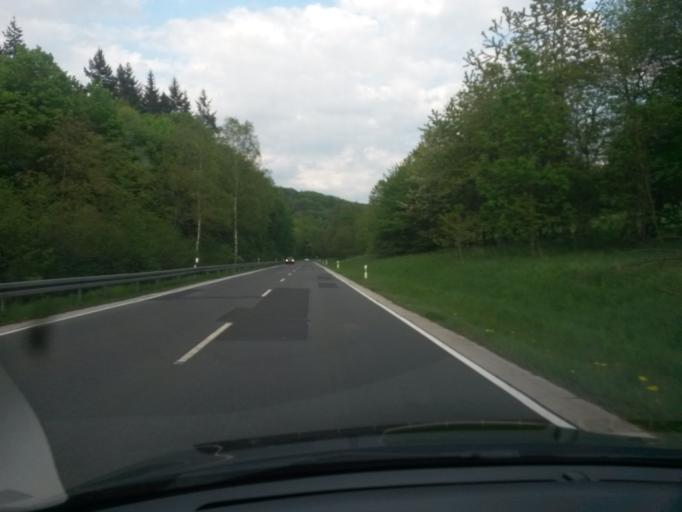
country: DE
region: Hesse
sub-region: Regierungsbezirk Kassel
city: Baunatal
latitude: 51.3092
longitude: 9.3830
